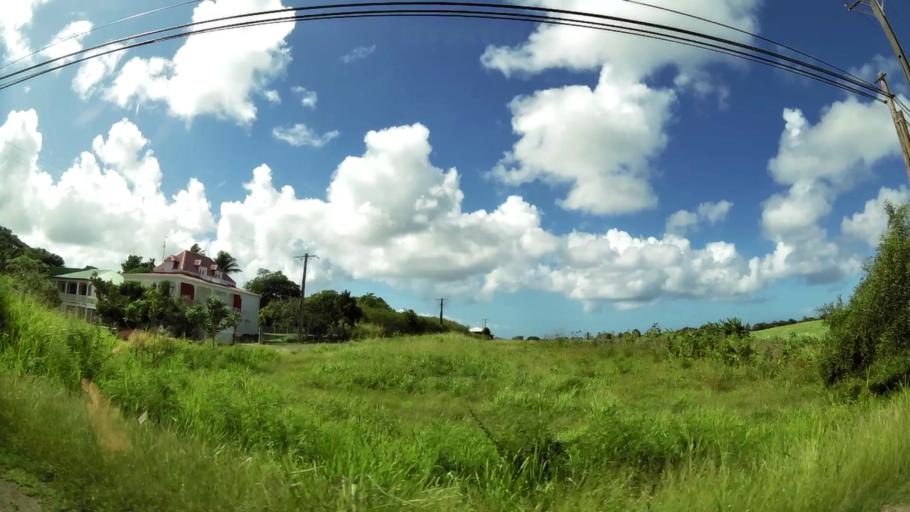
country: GP
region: Guadeloupe
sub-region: Guadeloupe
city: Anse-Bertrand
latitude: 16.4596
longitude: -61.4818
